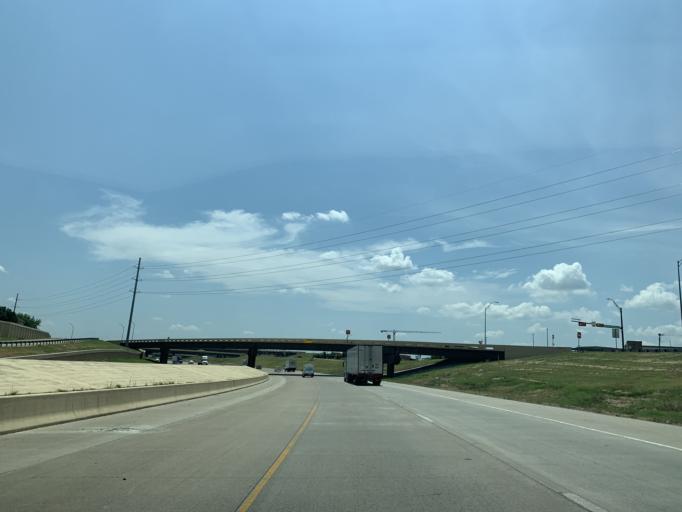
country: US
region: Texas
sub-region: Denton County
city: Roanoke
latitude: 33.0024
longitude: -97.2177
